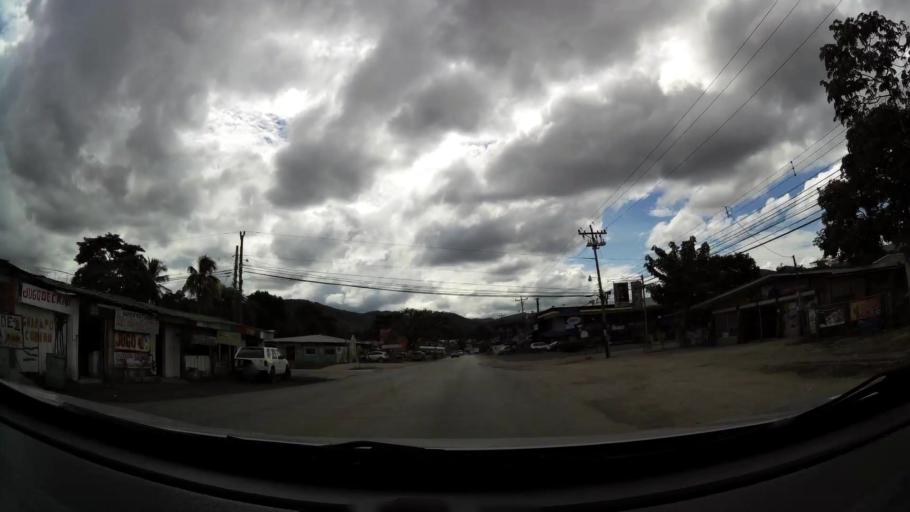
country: CR
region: Guanacaste
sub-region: Canton de Nicoya
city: Nicoya
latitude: 10.1518
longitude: -85.4517
